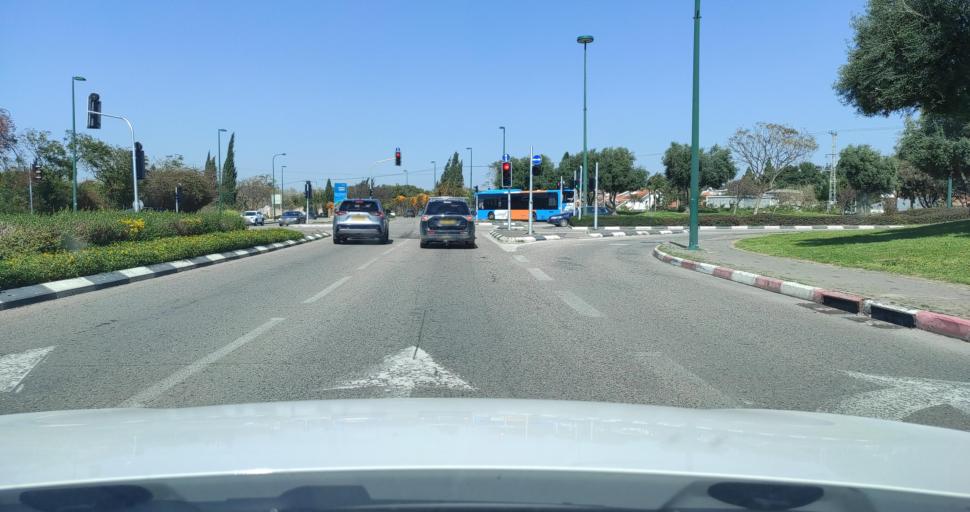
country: IL
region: Central District
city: Bet Yizhaq
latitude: 32.3170
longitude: 34.8815
